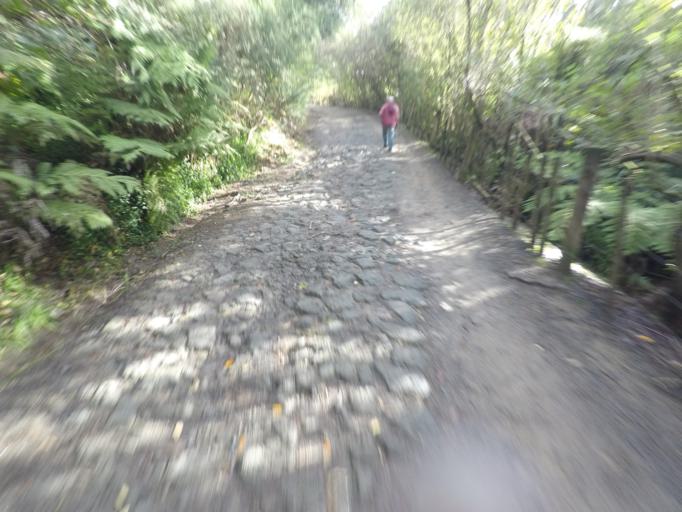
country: NZ
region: Auckland
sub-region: Auckland
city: Manukau City
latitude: -36.9996
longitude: 174.9116
